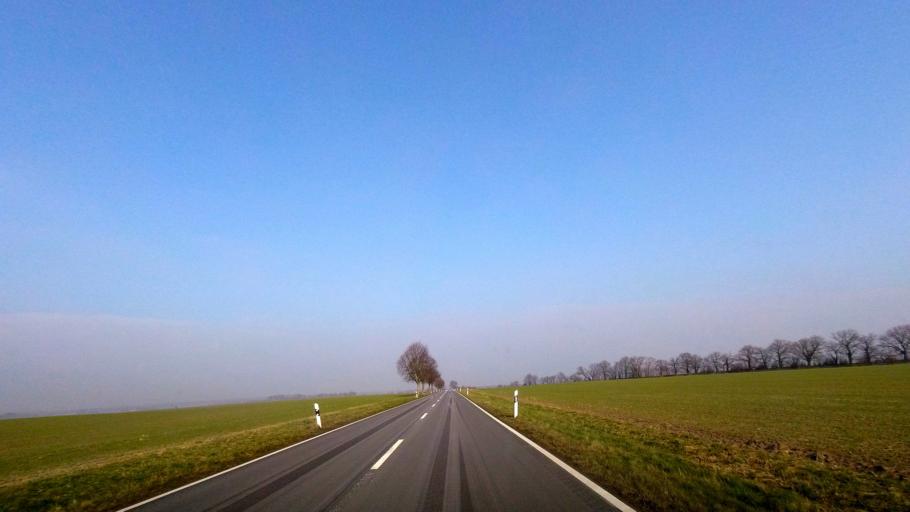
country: DE
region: Brandenburg
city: Niedergorsdorf
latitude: 51.9443
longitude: 13.0388
